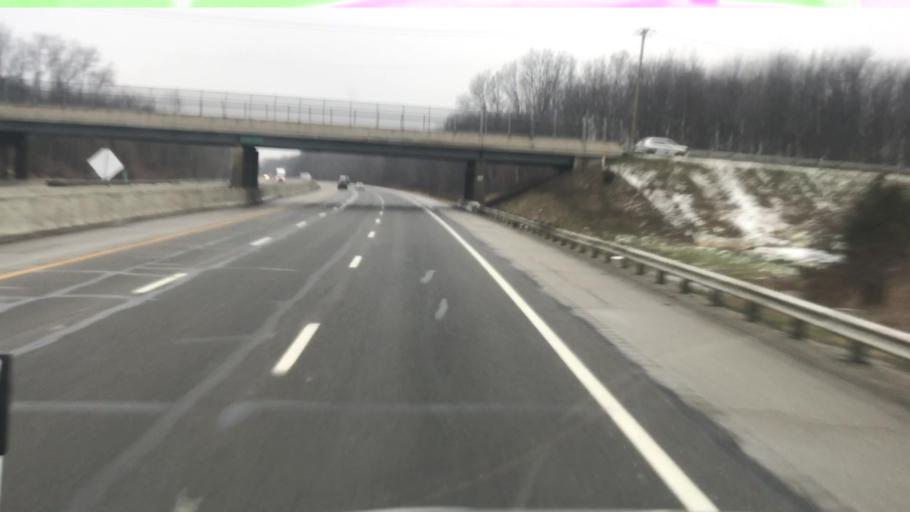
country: US
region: Ohio
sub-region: Cuyahoga County
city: Olmsted Falls
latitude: 41.3695
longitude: -81.9435
